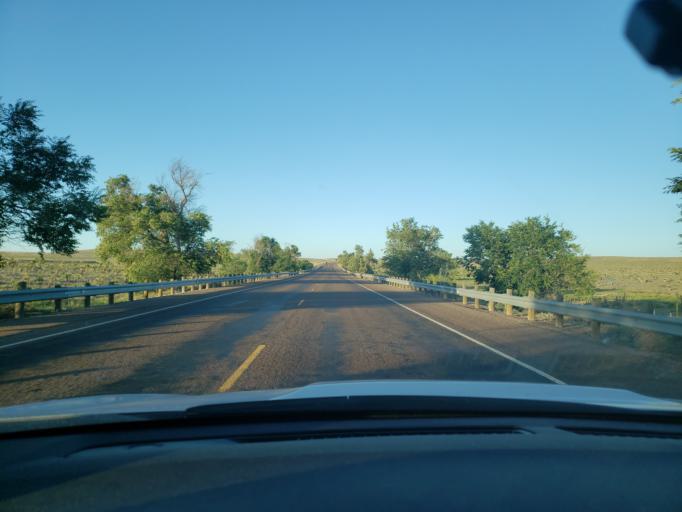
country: US
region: Texas
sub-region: El Paso County
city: Homestead Meadows South
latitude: 31.8313
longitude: -105.8645
